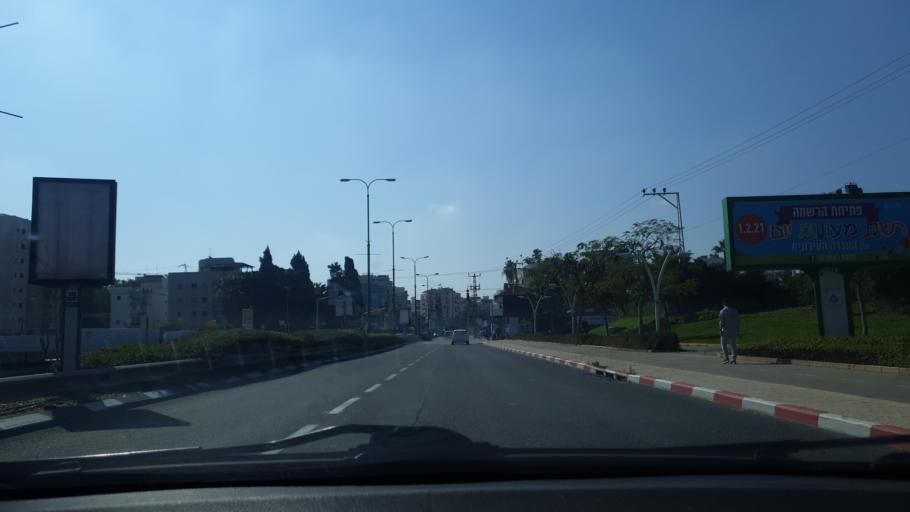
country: IL
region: Central District
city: Rishon LeZiyyon
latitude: 31.9745
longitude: 34.8071
